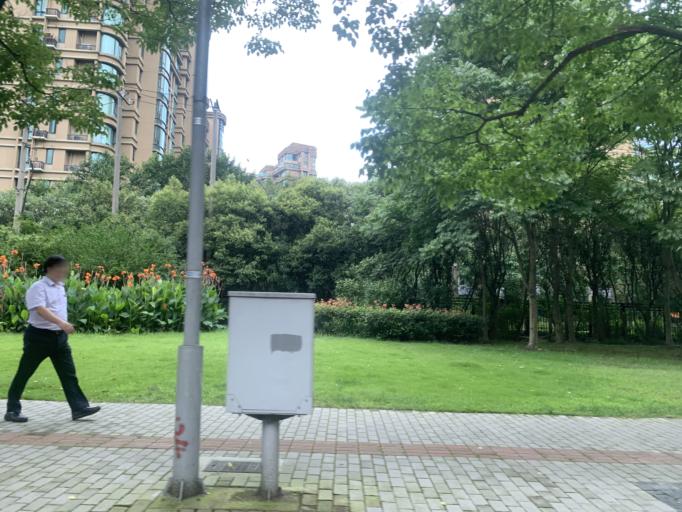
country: CN
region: Shanghai Shi
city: Huamu
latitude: 31.2074
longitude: 121.5316
